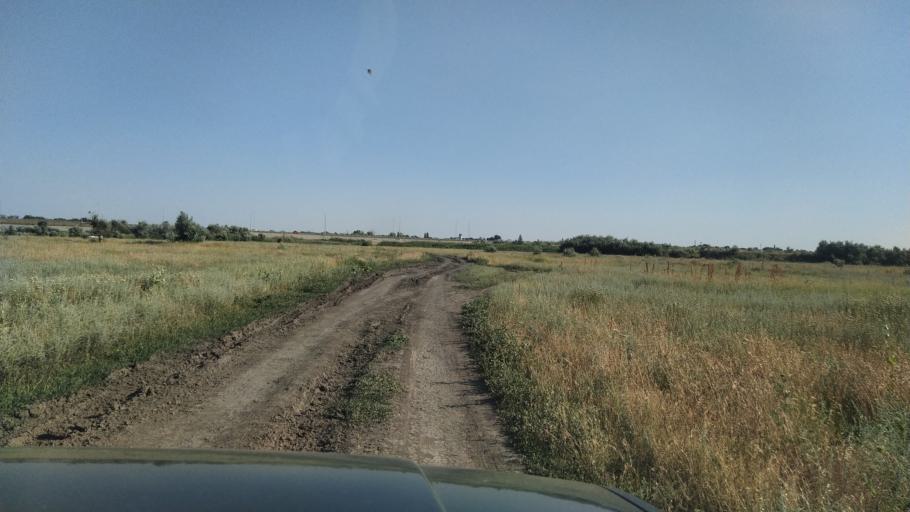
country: RU
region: Rostov
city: Kuleshovka
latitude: 47.1214
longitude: 39.6490
